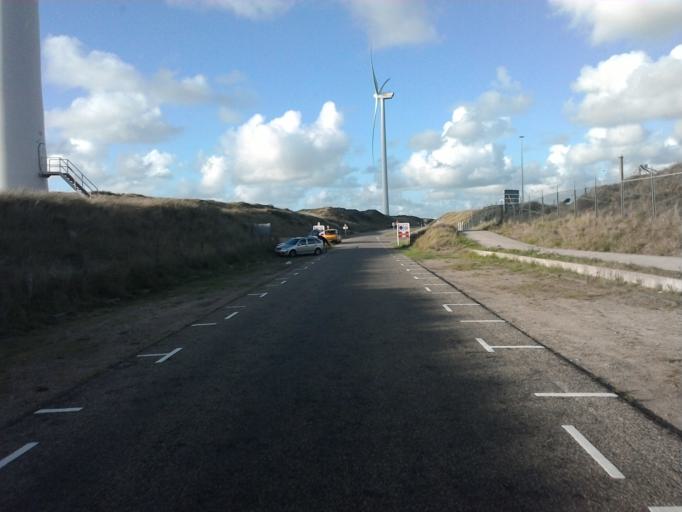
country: NL
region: North Holland
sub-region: Gemeente Velsen
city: Velsen-Zuid
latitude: 52.4724
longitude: 4.5747
